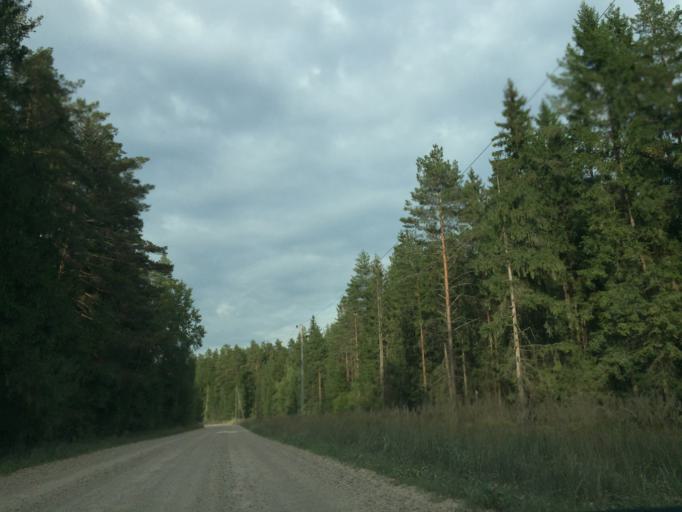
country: LV
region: Ikskile
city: Ikskile
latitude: 56.8008
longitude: 24.4380
